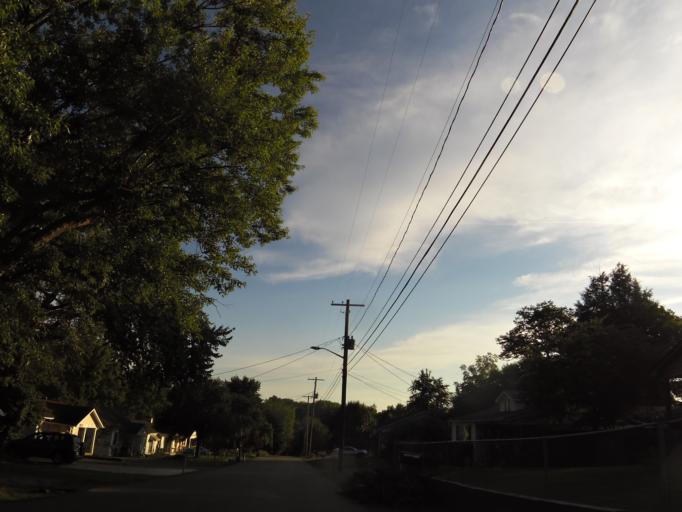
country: US
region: Tennessee
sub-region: Knox County
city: Knoxville
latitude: 35.9262
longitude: -83.9191
